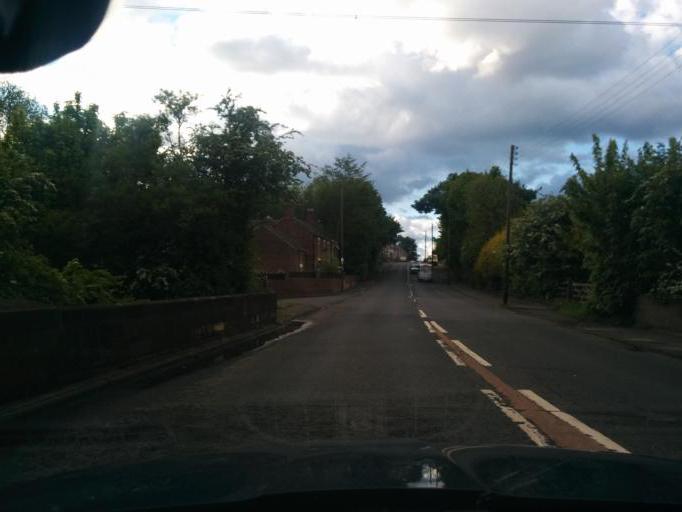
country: GB
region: England
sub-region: Northumberland
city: Choppington
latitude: 55.1465
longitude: -1.6005
